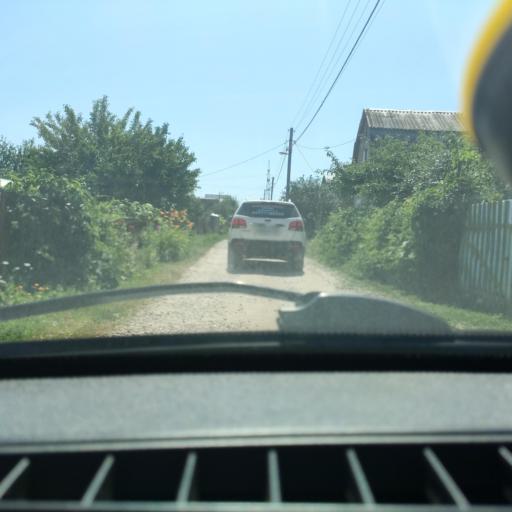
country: RU
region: Samara
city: Tol'yatti
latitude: 53.5924
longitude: 49.3048
